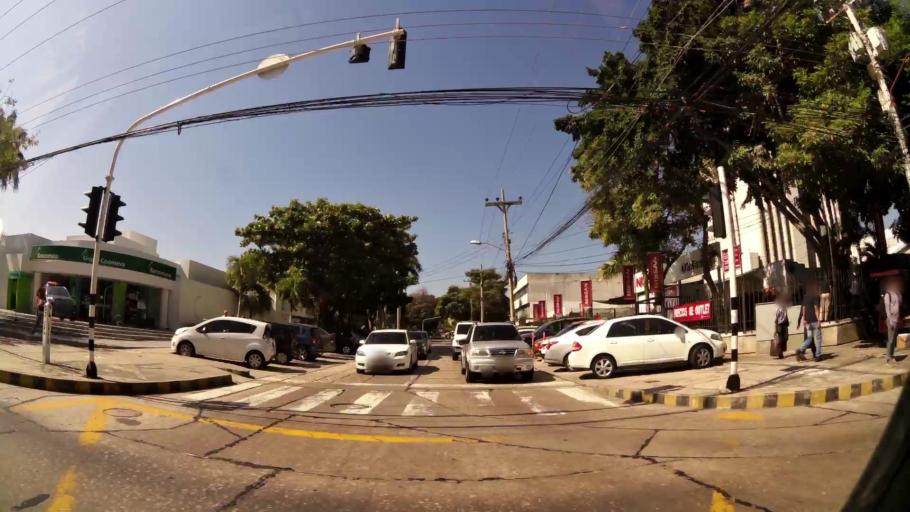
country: CO
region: Atlantico
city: Barranquilla
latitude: 10.9998
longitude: -74.8036
